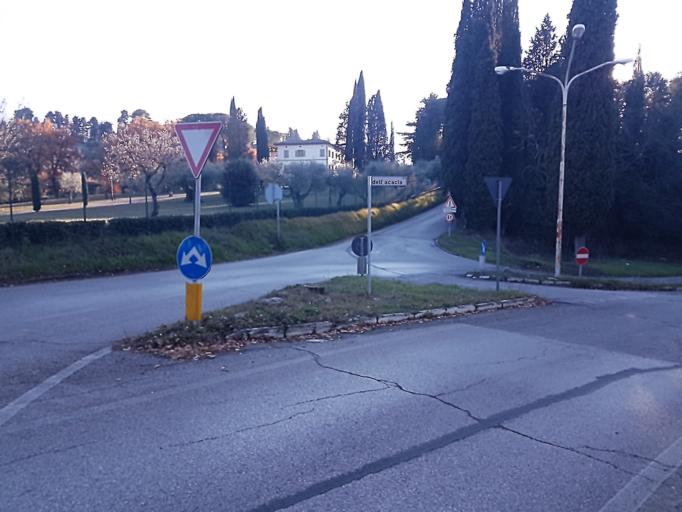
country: IT
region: Umbria
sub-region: Provincia di Perugia
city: Perugia
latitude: 43.0926
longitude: 12.3781
